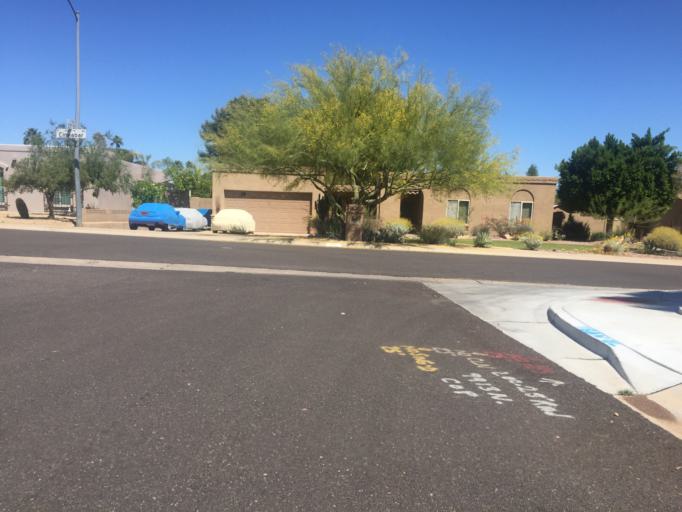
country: US
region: Arizona
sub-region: Maricopa County
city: Paradise Valley
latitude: 33.5763
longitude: -112.0280
